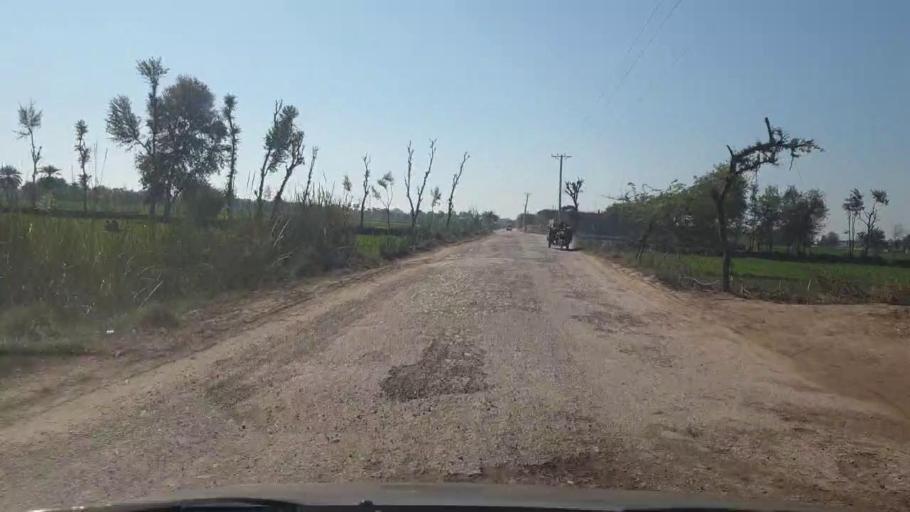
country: PK
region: Sindh
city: Bozdar
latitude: 27.0805
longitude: 68.6190
